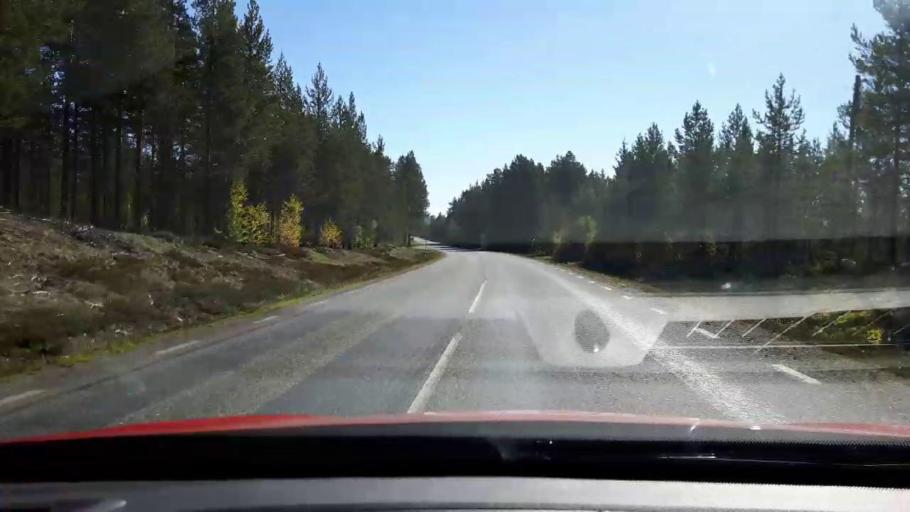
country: SE
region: Jaemtland
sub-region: Harjedalens Kommun
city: Sveg
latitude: 62.3586
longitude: 14.0092
